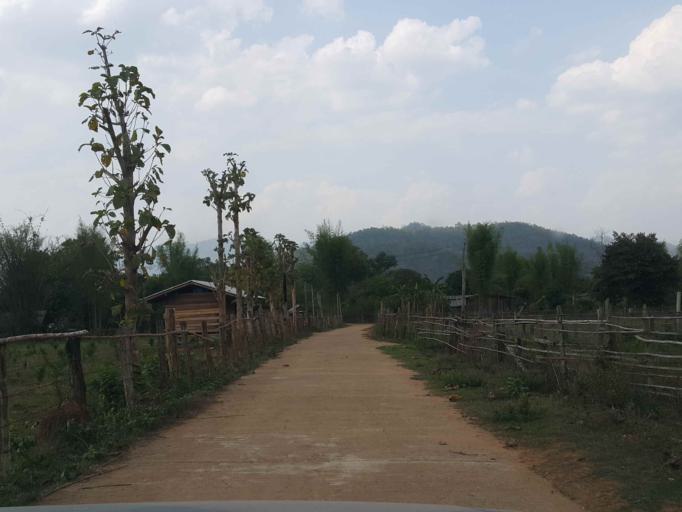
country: TH
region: Chiang Mai
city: Wiang Haeng
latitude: 19.3753
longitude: 98.7211
